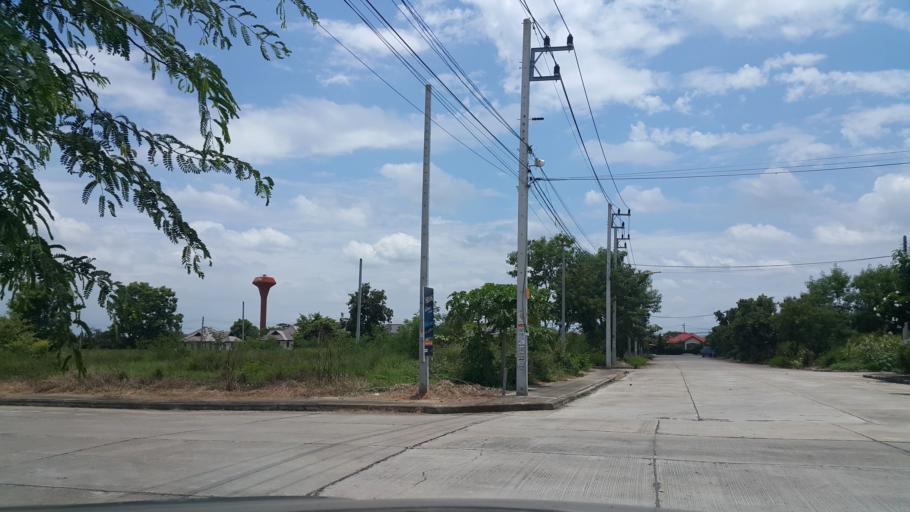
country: TH
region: Chiang Mai
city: Hang Dong
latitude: 18.7080
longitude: 98.9732
